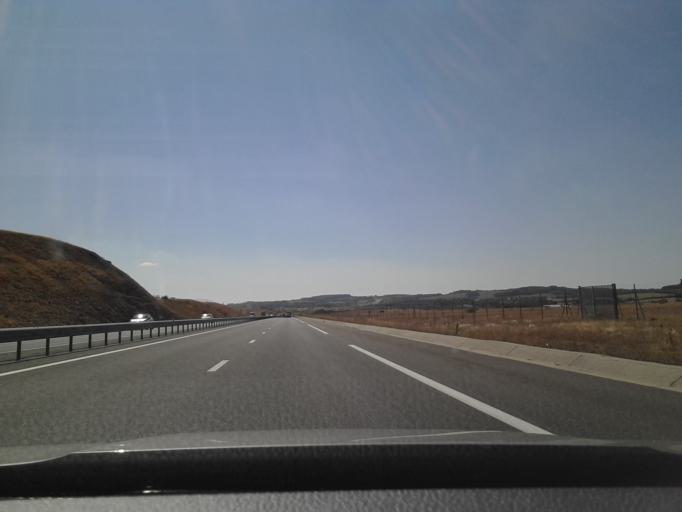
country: FR
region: Midi-Pyrenees
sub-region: Departement de l'Aveyron
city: La Cavalerie
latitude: 44.0226
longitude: 3.1218
